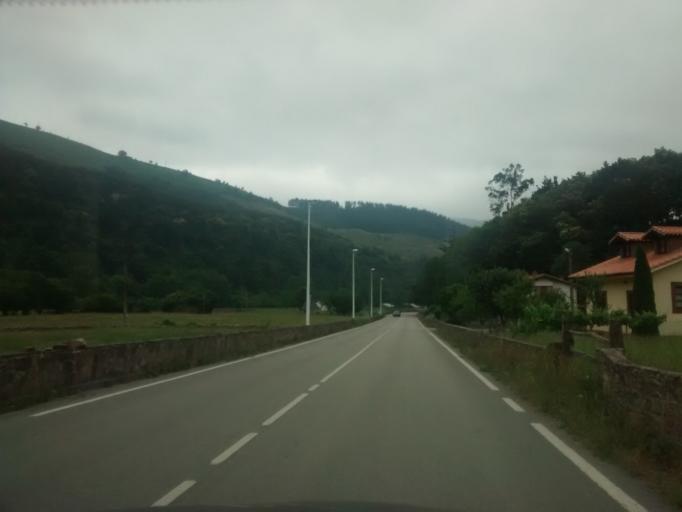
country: ES
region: Cantabria
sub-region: Provincia de Cantabria
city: Ruente
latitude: 43.2426
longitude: -4.2849
